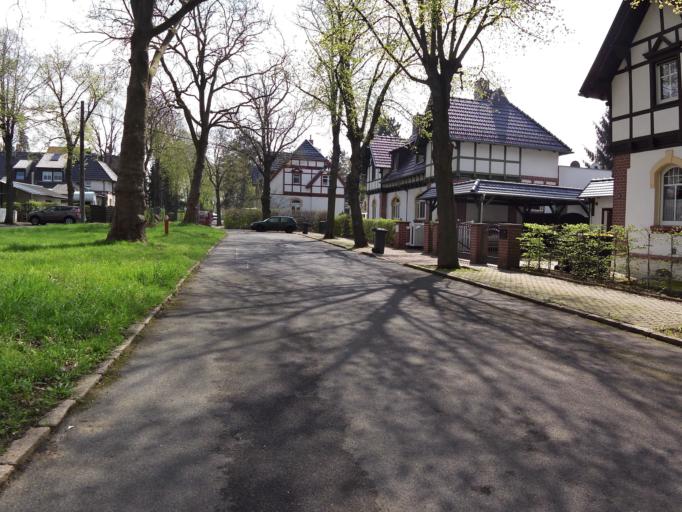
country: DE
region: Saxony
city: Markranstadt
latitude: 51.3272
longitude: 12.2517
